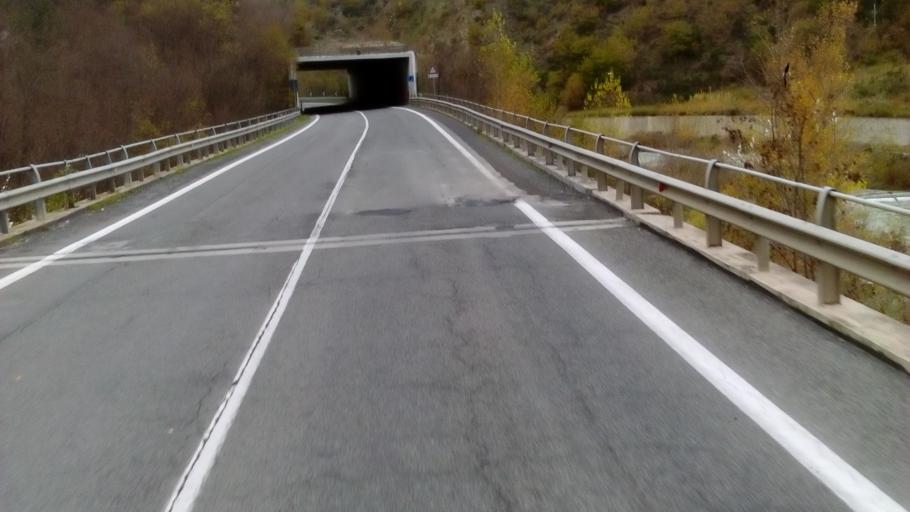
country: IT
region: Molise
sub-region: Provincia di Campobasso
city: Trivento
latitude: 41.7904
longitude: 14.5356
